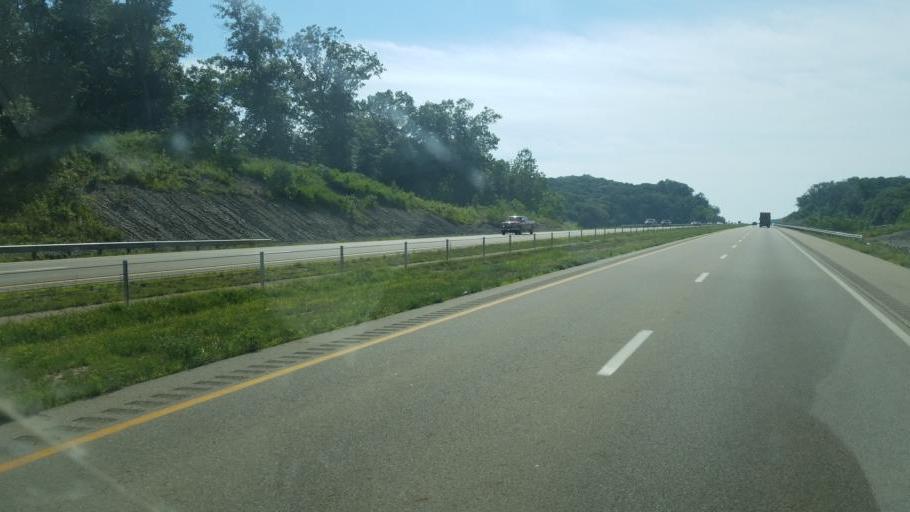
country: US
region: Ohio
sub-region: Athens County
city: Nelsonville
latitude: 39.4740
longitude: -82.2813
